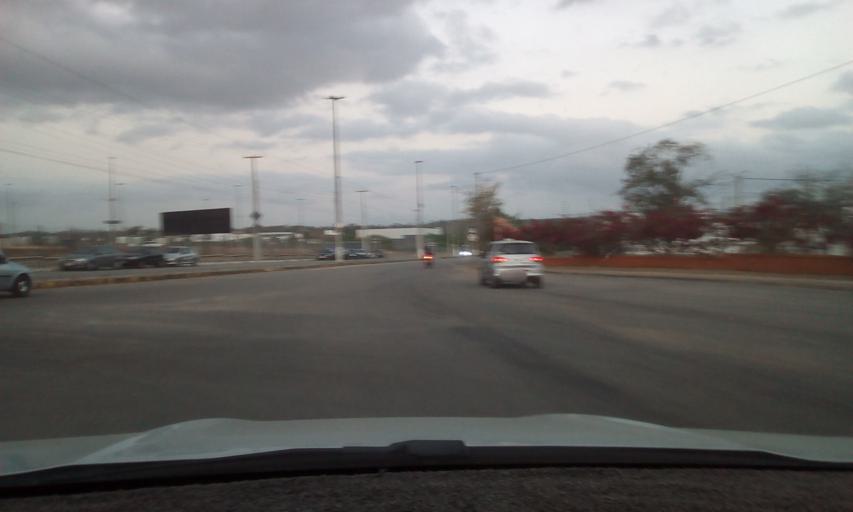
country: BR
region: Pernambuco
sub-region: Caruaru
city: Caruaru
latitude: -8.2422
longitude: -35.9804
